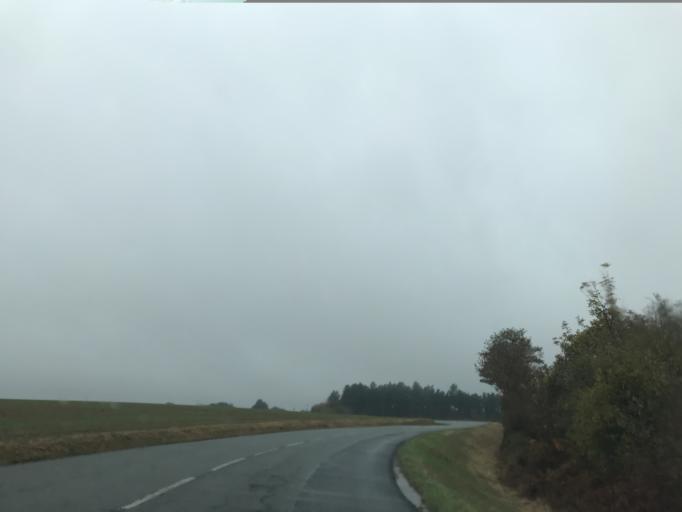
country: FR
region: Auvergne
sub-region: Departement du Puy-de-Dome
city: Courpiere
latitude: 45.7707
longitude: 3.5109
